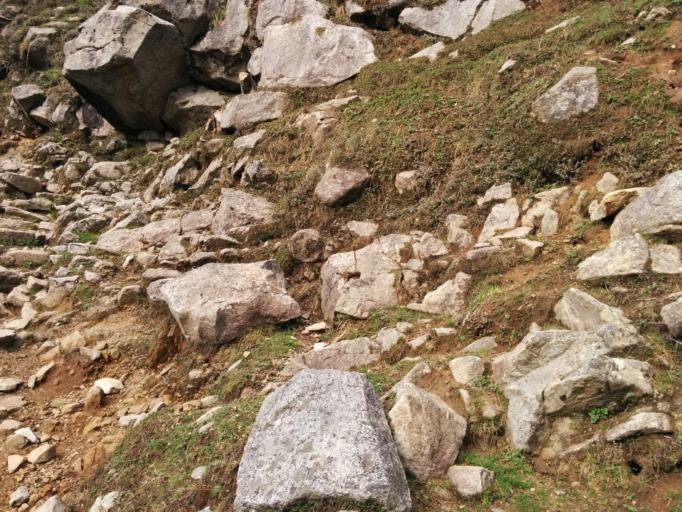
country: IN
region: Himachal Pradesh
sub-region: Kangra
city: Dharmsala
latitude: 32.2807
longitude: 76.3634
